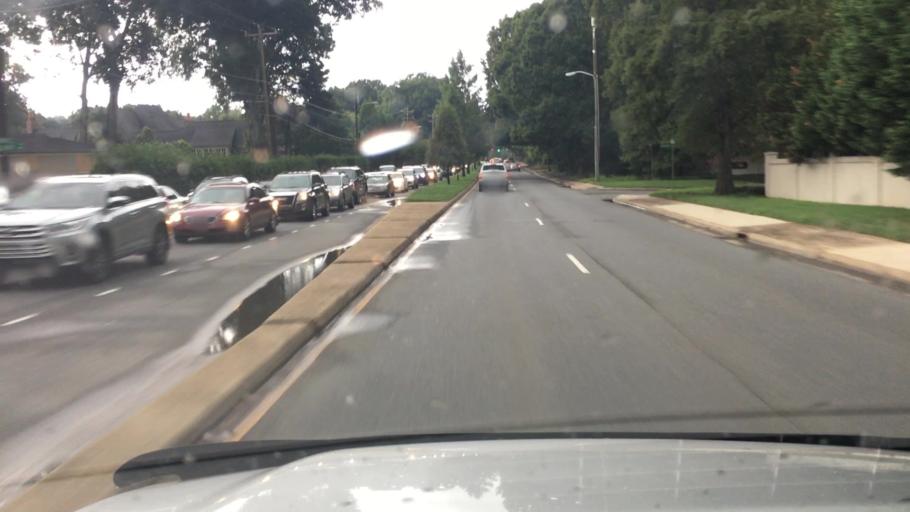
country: US
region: North Carolina
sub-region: Mecklenburg County
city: Matthews
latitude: 35.1512
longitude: -80.7984
